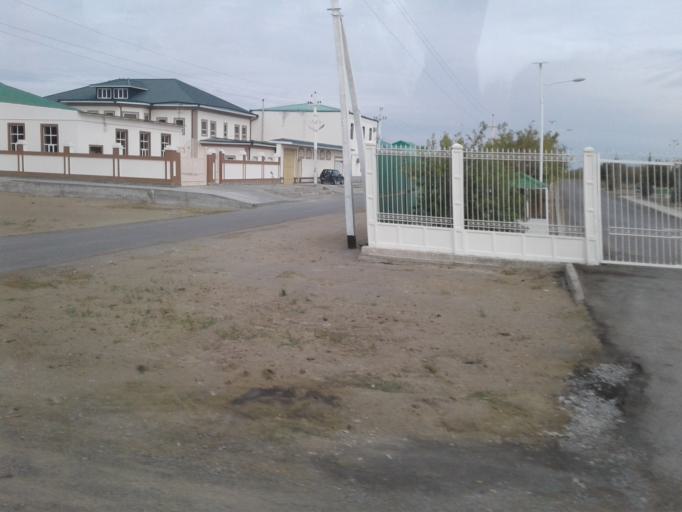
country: TM
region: Lebap
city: Turkmenabat
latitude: 38.9918
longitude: 63.5559
